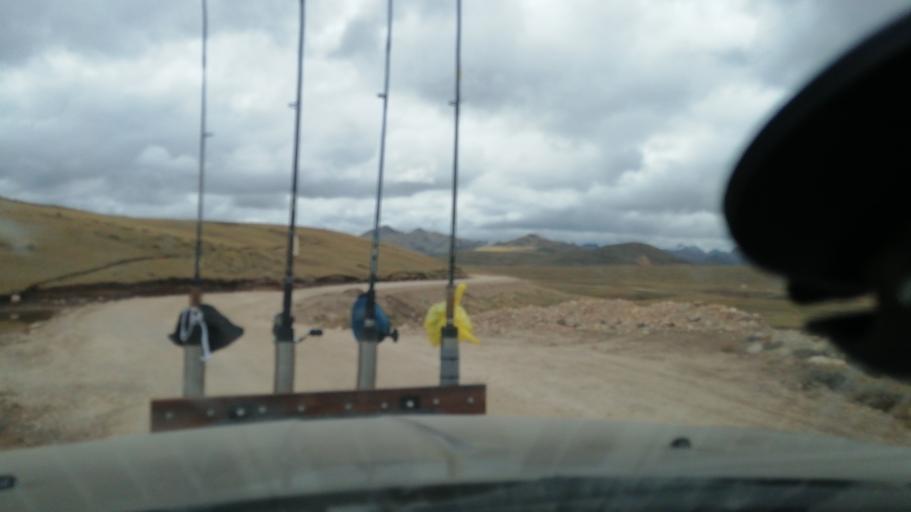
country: PE
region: Huancavelica
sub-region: Provincia de Huancavelica
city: Acobambilla
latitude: -12.5407
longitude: -75.5525
